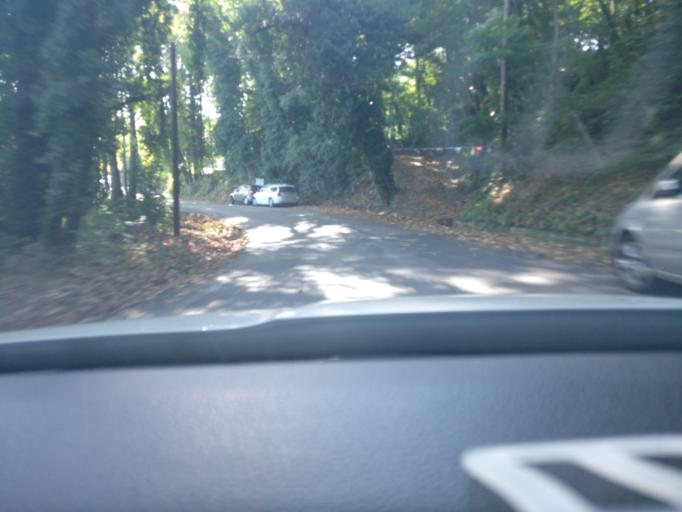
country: GR
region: Thessaly
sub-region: Nomos Magnisias
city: Zagora
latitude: 39.3843
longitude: 23.1795
